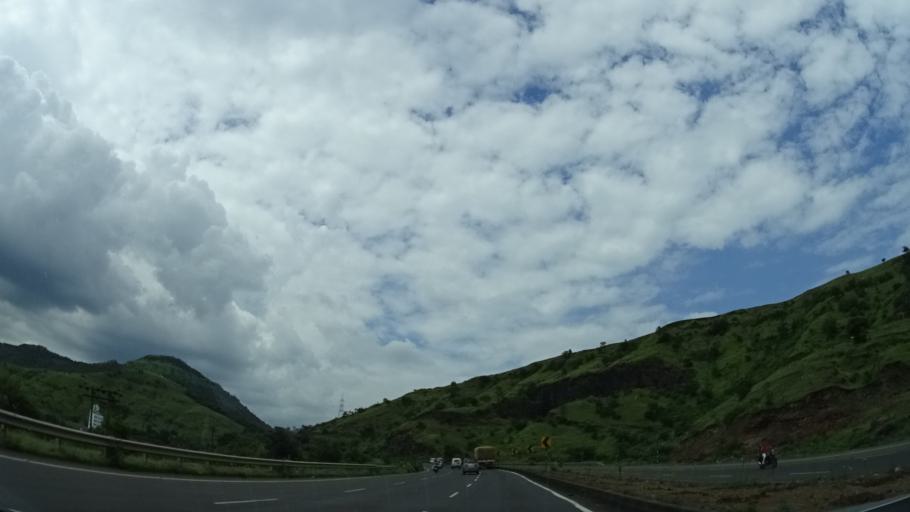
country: IN
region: Maharashtra
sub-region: Satara Division
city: Satara
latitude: 17.6500
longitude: 74.0135
